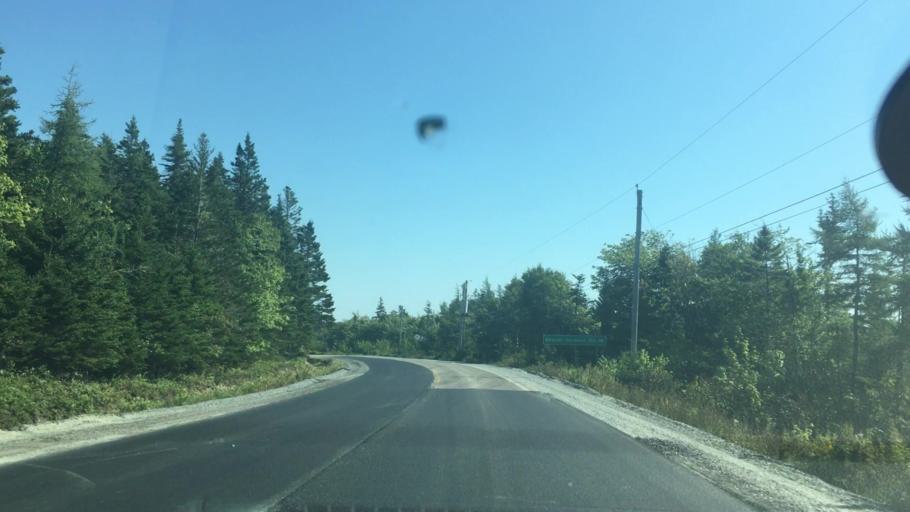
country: CA
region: Nova Scotia
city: New Glasgow
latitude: 44.8983
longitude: -62.4220
